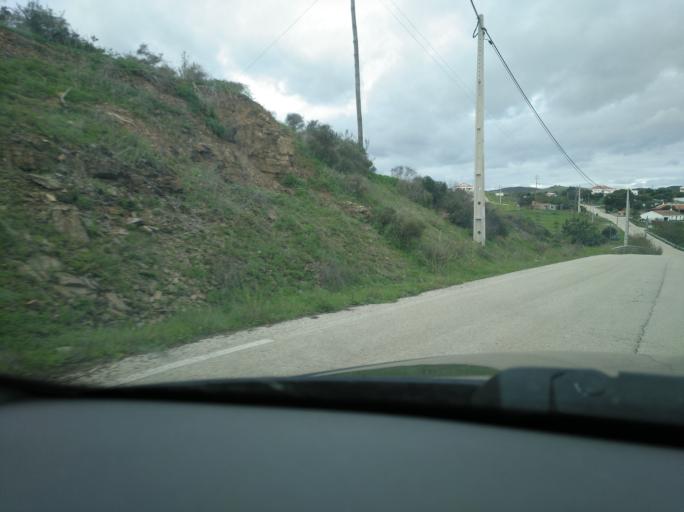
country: PT
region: Faro
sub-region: Castro Marim
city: Castro Marim
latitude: 37.2166
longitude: -7.4874
